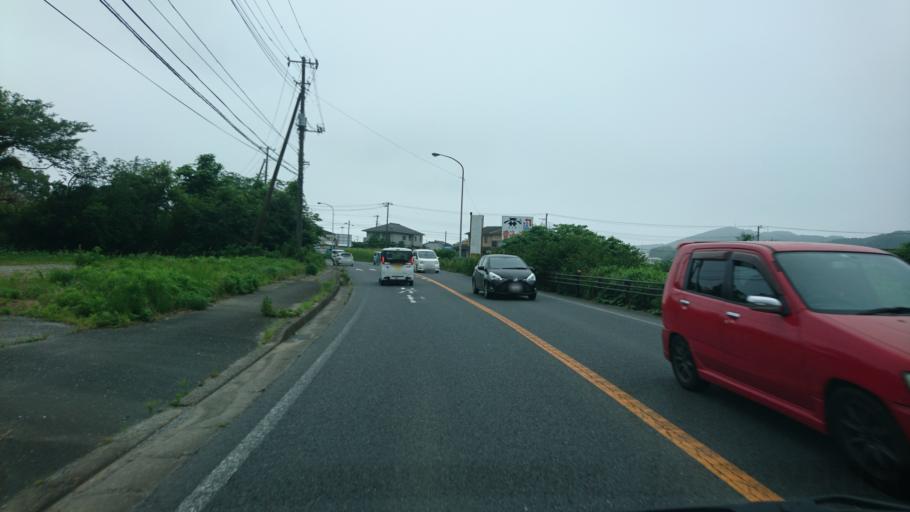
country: JP
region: Chiba
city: Kimitsu
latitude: 35.2637
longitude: 139.8863
